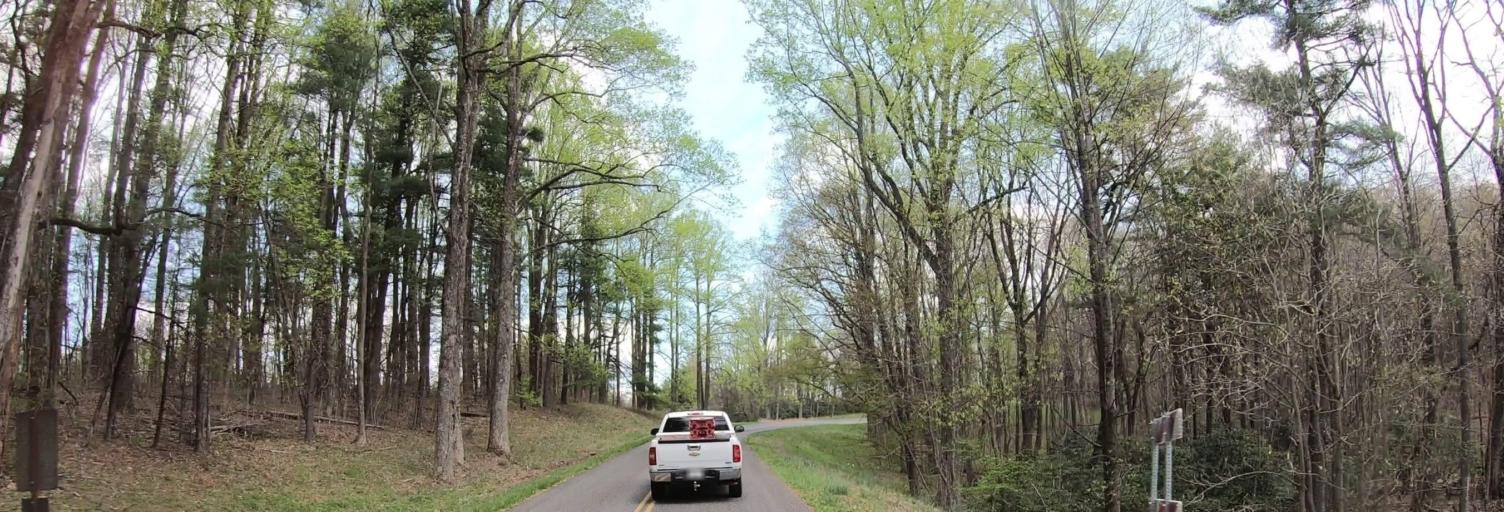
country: US
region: Virginia
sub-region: Carroll County
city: Cana
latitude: 36.6606
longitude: -80.6999
